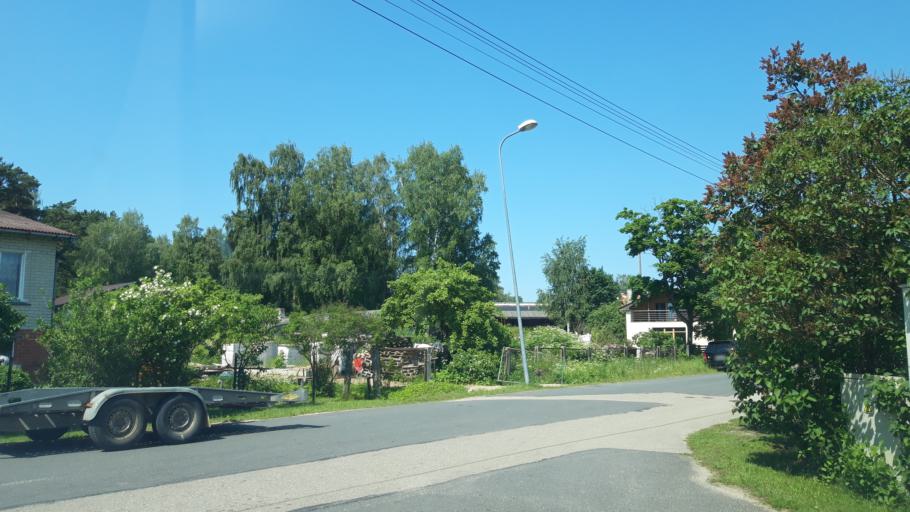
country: LV
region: Saulkrastu
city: Saulkrasti
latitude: 57.2548
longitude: 24.4164
